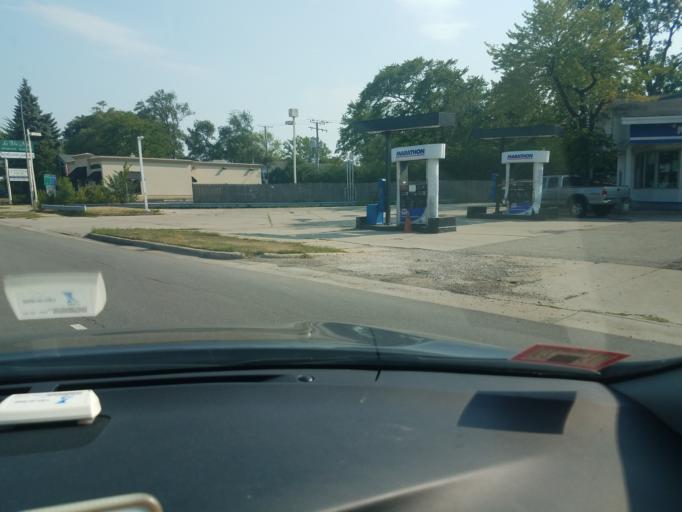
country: US
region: Illinois
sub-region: Cook County
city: Northbrook
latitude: 42.1381
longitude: -87.8252
